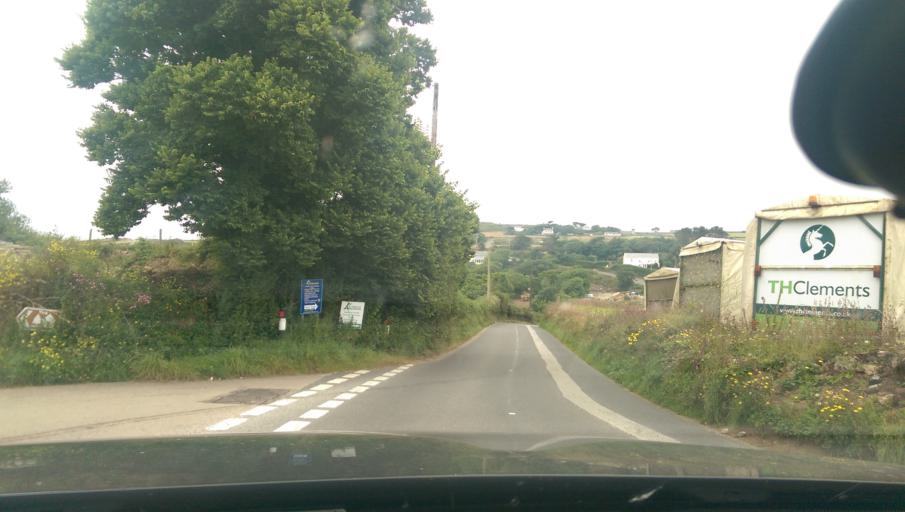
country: GB
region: England
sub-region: Cornwall
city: Saint Just
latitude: 50.1113
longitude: -5.6783
